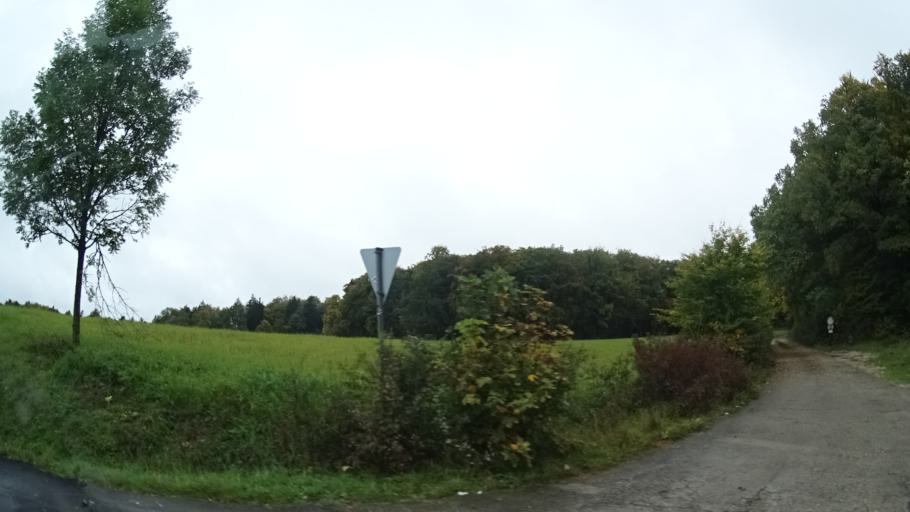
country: DE
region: Bavaria
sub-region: Upper Franconia
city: Wattendorf
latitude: 50.0418
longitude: 11.1306
